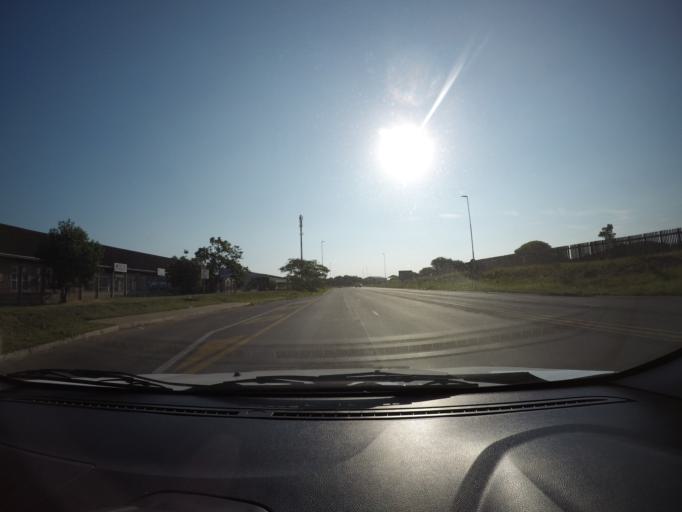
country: ZA
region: KwaZulu-Natal
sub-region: uThungulu District Municipality
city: Richards Bay
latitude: -28.7324
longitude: 32.0376
